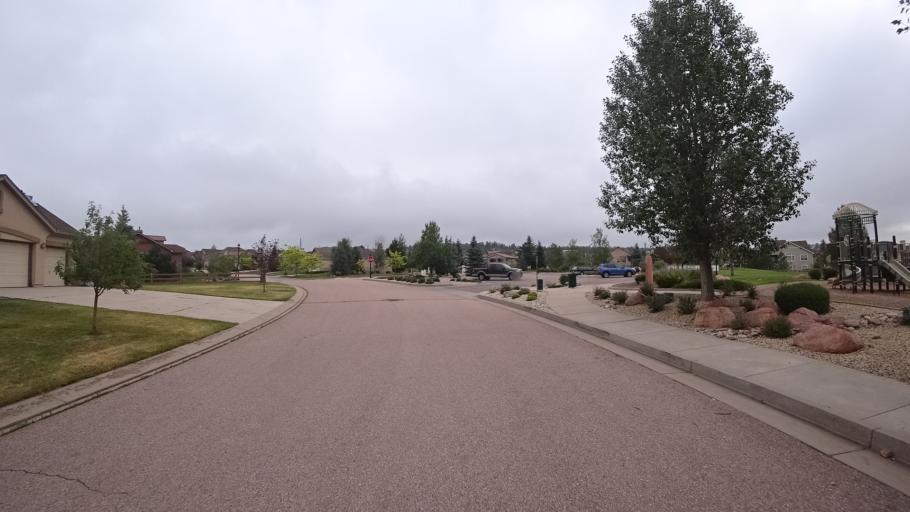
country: US
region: Colorado
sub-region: El Paso County
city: Gleneagle
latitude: 39.0307
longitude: -104.7830
